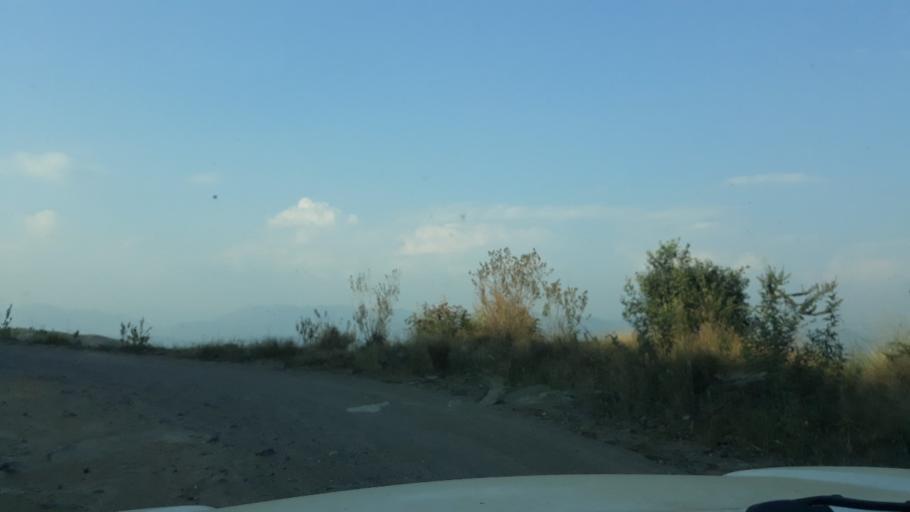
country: BI
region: Cibitoke
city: Cibitoke
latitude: -2.7038
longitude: 28.9860
